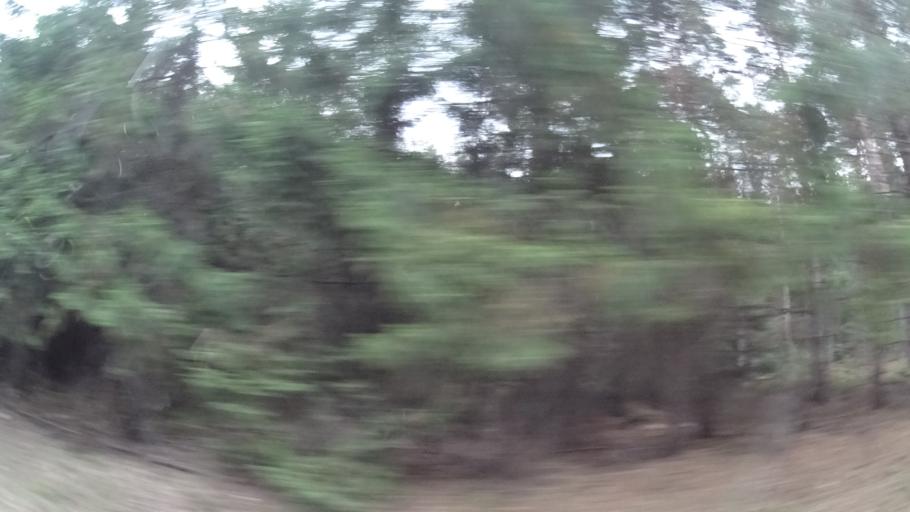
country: DE
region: Thuringia
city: Herschdorf
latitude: 50.6469
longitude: 11.0570
